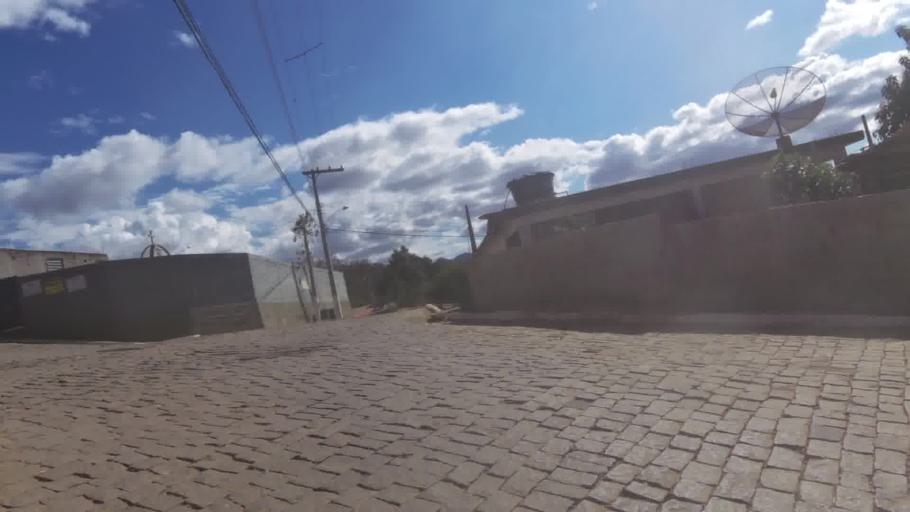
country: BR
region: Espirito Santo
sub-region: Cachoeiro De Itapemirim
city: Cachoeiro de Itapemirim
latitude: -20.9184
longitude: -41.1957
